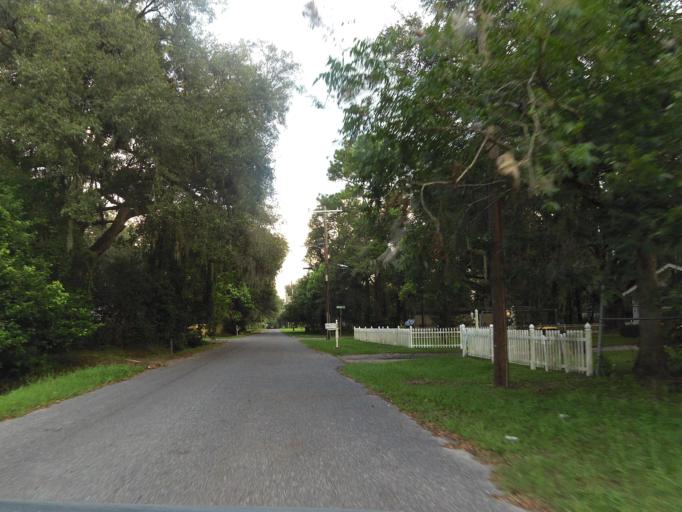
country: US
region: Florida
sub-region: Duval County
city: Jacksonville
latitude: 30.3307
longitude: -81.7860
